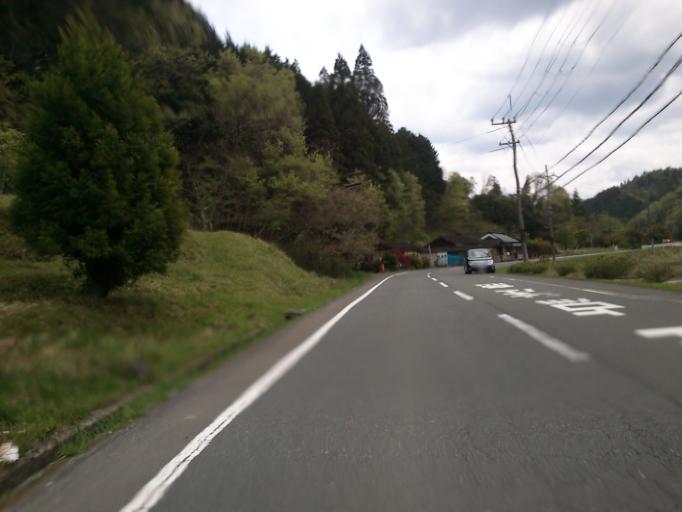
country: JP
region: Kyoto
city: Kameoka
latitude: 35.2102
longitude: 135.5720
